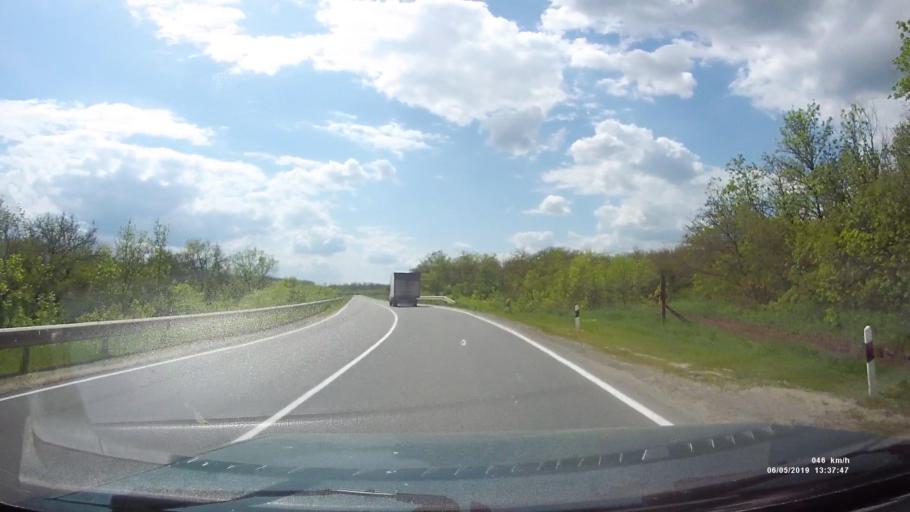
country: RU
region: Rostov
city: Ust'-Donetskiy
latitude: 47.6891
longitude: 40.7159
